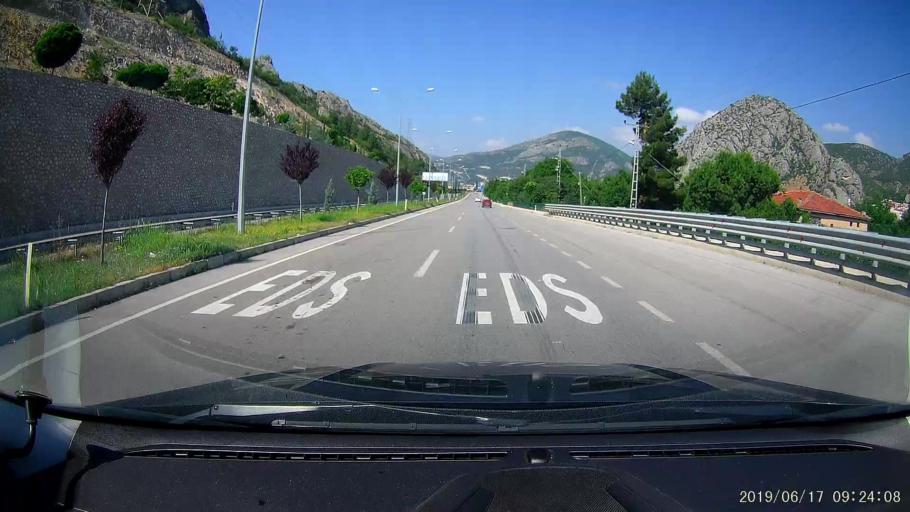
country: TR
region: Amasya
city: Amasya
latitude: 40.6735
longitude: 35.8613
